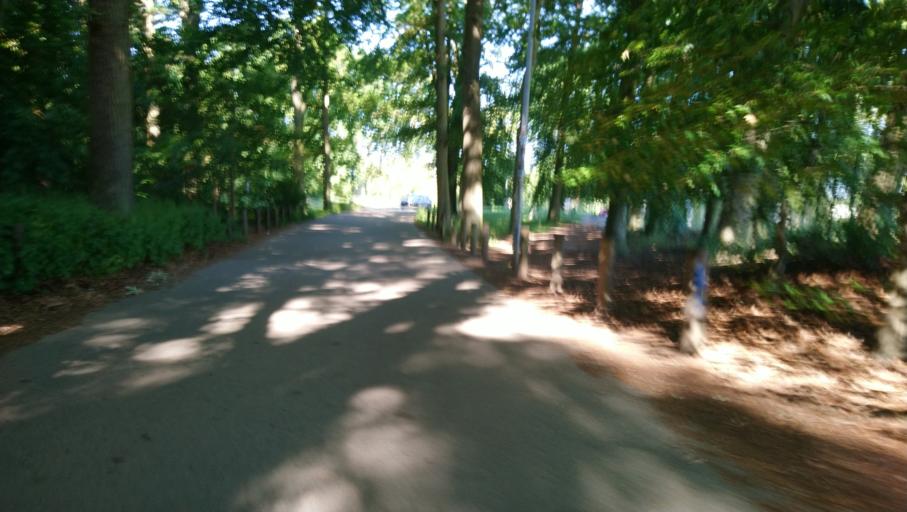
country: DE
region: Mecklenburg-Vorpommern
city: Kritzmow
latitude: 54.0829
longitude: 12.0887
